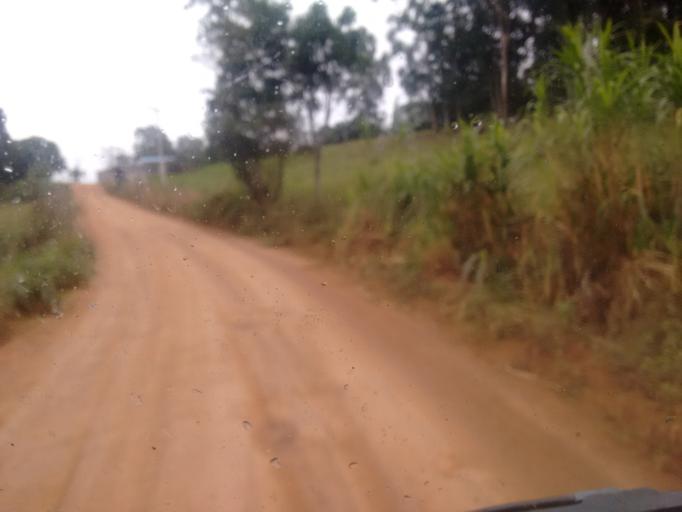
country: BR
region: Rio Grande do Sul
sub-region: Camaqua
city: Camaqua
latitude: -30.7266
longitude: -51.8473
